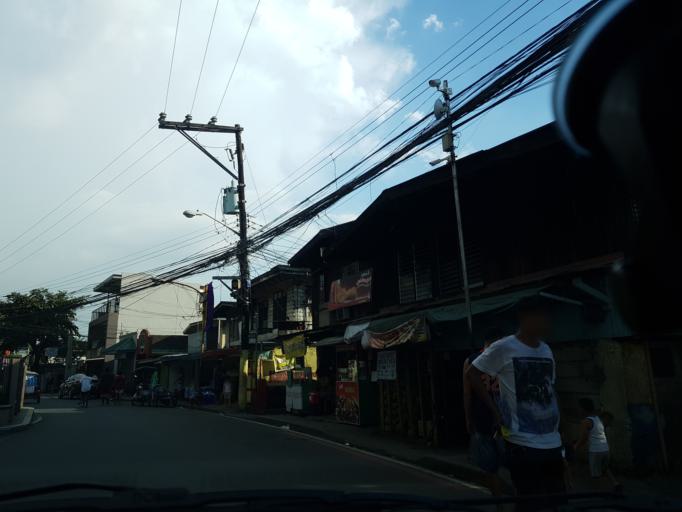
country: PH
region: Metro Manila
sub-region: Marikina
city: Calumpang
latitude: 14.6152
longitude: 121.0818
